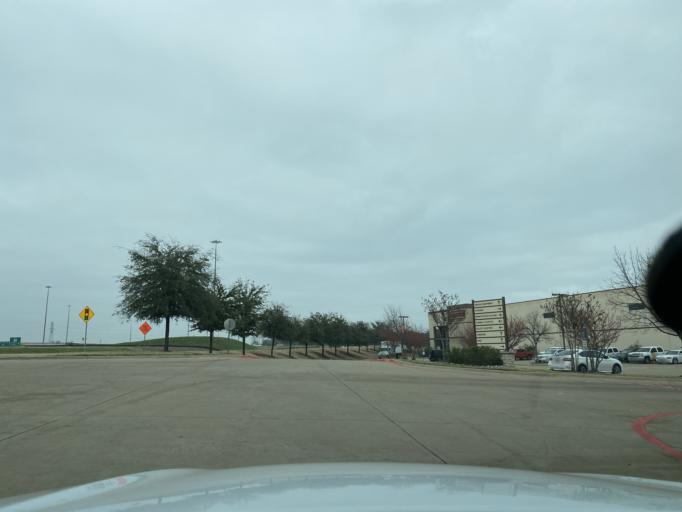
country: US
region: Texas
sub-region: Tarrant County
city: Arlington
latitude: 32.7100
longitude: -97.0612
